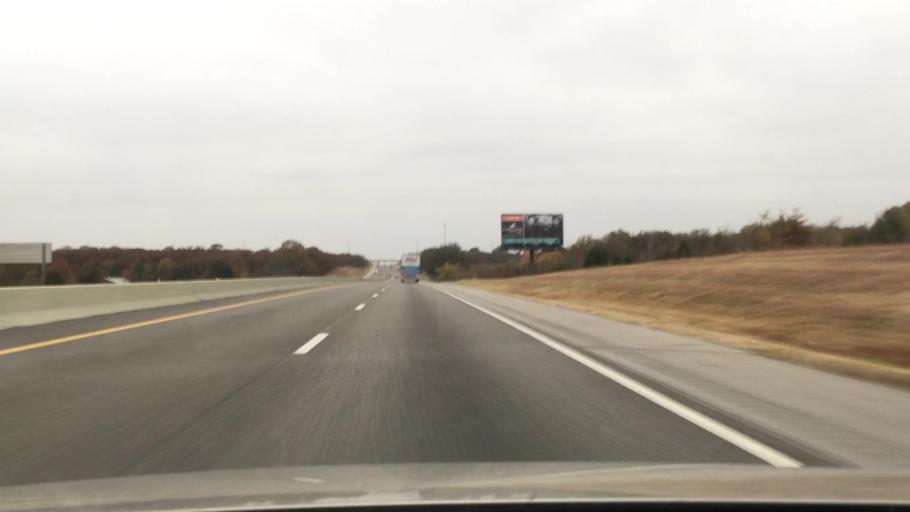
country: US
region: Oklahoma
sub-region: Lincoln County
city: Chandler
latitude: 35.7248
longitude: -96.8550
